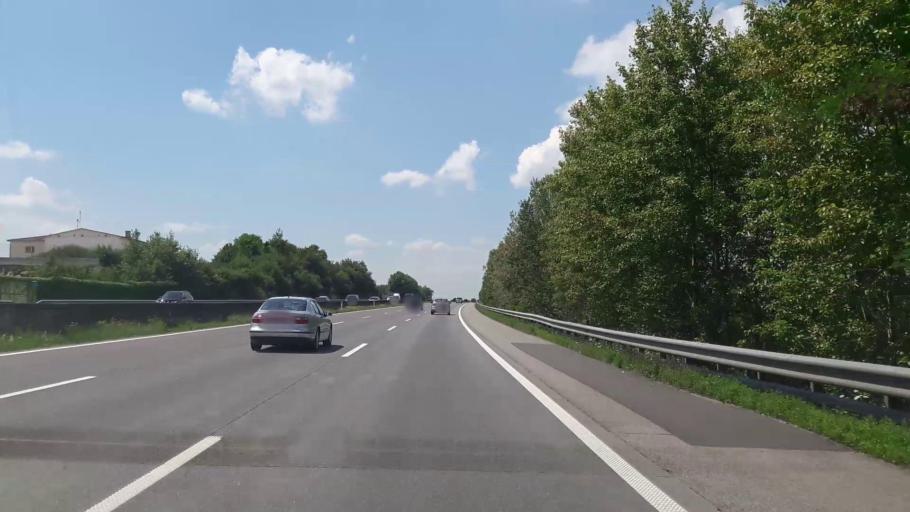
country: AT
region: Lower Austria
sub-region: Politischer Bezirk Amstetten
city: Zeillern
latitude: 48.1194
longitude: 14.7751
